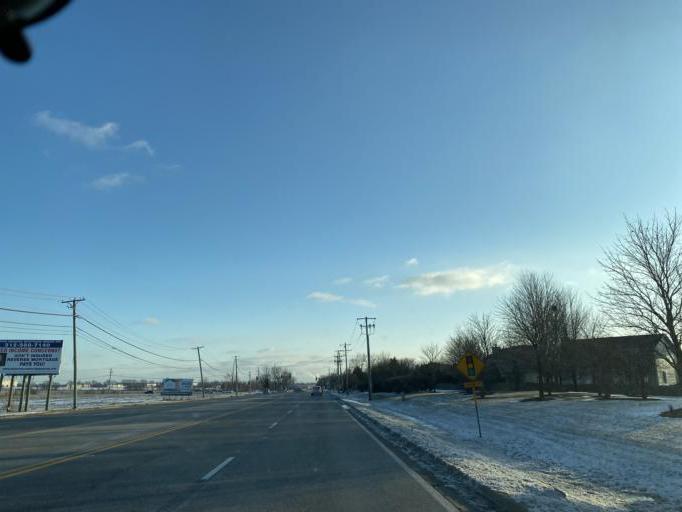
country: US
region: Illinois
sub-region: Will County
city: Romeoville
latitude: 41.6266
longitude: -88.1239
